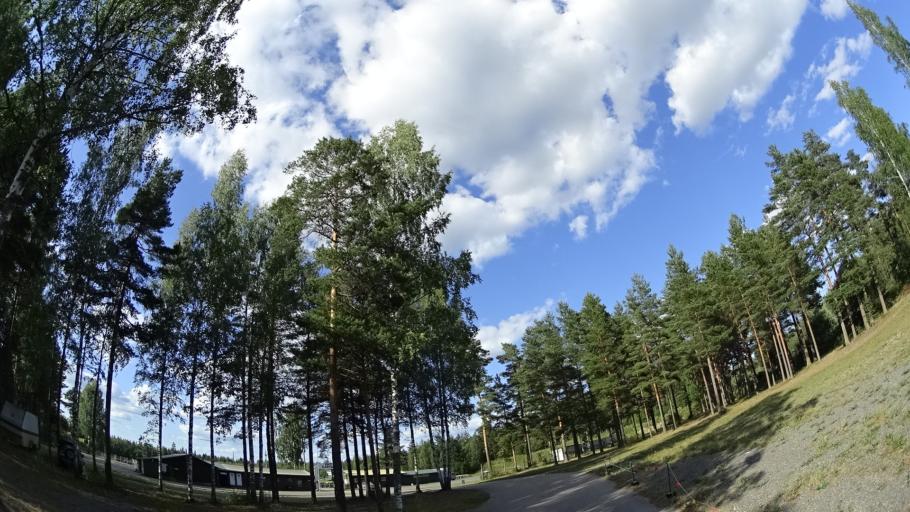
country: FI
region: Uusimaa
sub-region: Helsinki
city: Vihti
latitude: 60.3629
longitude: 24.3538
